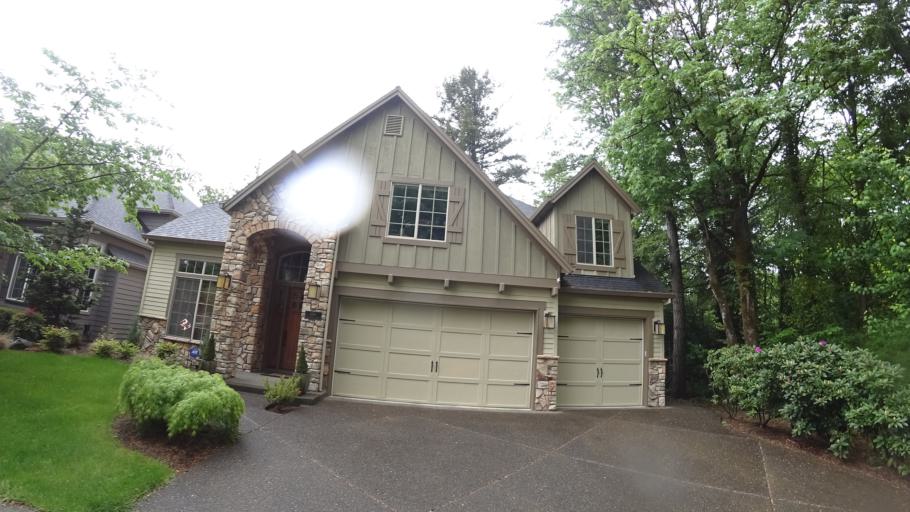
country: US
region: Oregon
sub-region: Washington County
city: West Haven
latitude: 45.5303
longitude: -122.7646
